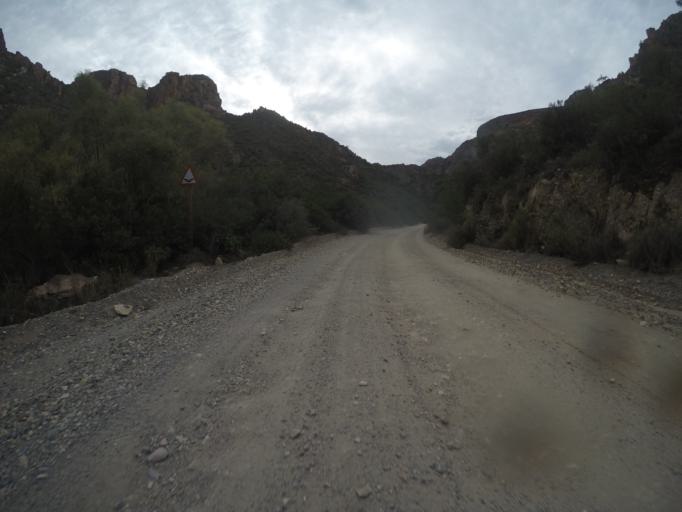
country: ZA
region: Eastern Cape
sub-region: Cacadu District Municipality
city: Willowmore
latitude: -33.5145
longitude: 23.6439
